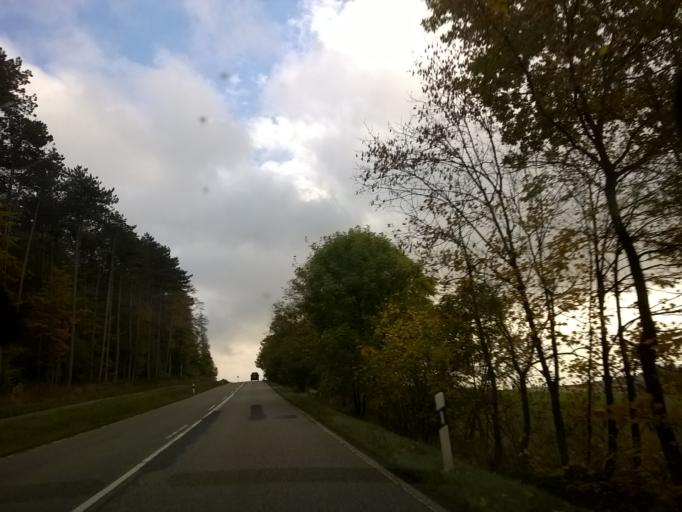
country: DE
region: Thuringia
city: Sondershausen
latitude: 51.3286
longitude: 10.8387
